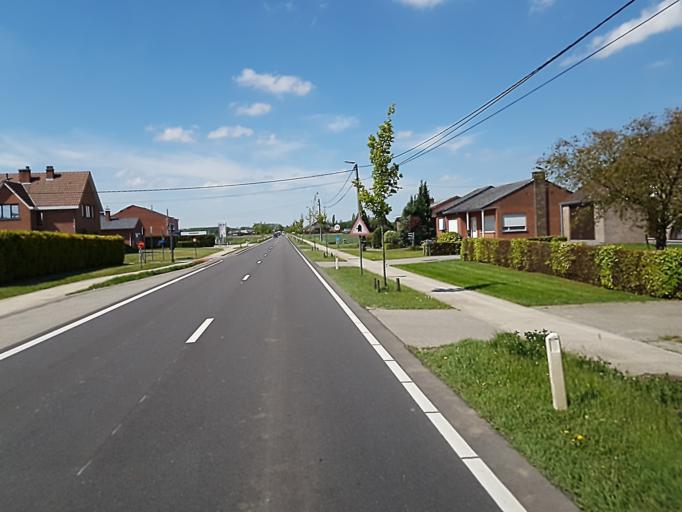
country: BE
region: Flanders
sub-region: Provincie Vlaams-Brabant
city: Glabbeek-Zuurbemde
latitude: 50.8586
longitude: 4.8970
